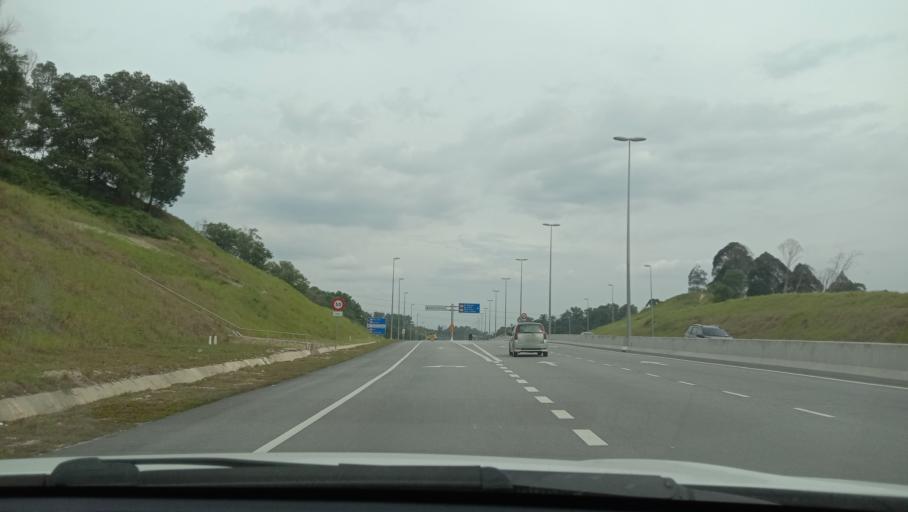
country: MY
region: Selangor
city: Kampung Baru Subang
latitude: 3.1266
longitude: 101.5157
